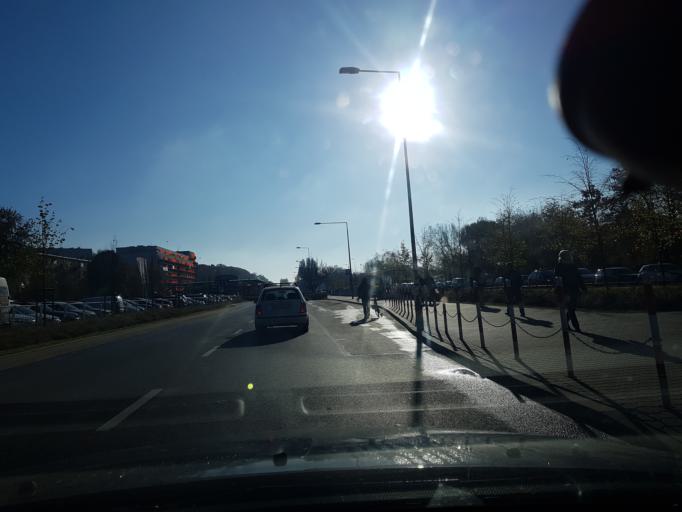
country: PL
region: Masovian Voivodeship
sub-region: Warszawa
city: Bielany
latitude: 52.2876
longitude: 20.9362
